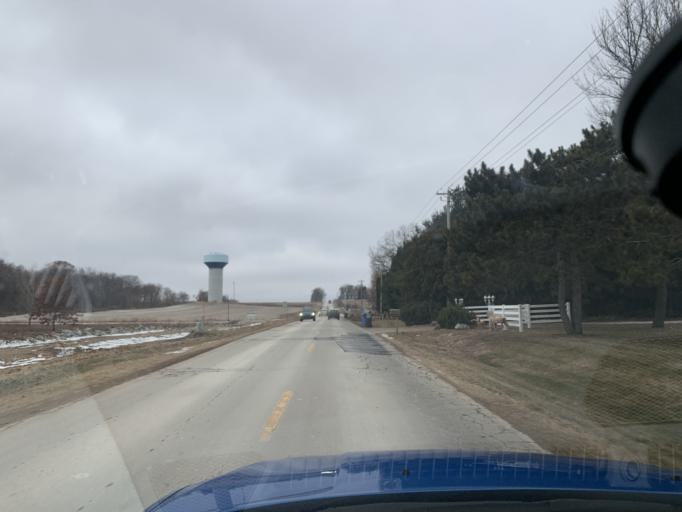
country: US
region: Wisconsin
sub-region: Dane County
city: Middleton
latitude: 43.0747
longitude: -89.5615
